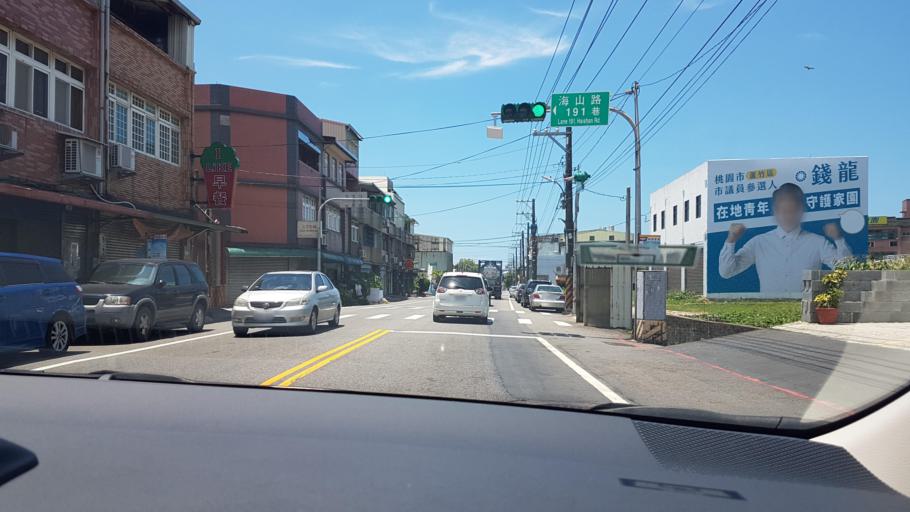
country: TW
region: Taiwan
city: Taoyuan City
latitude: 25.0868
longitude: 121.2821
